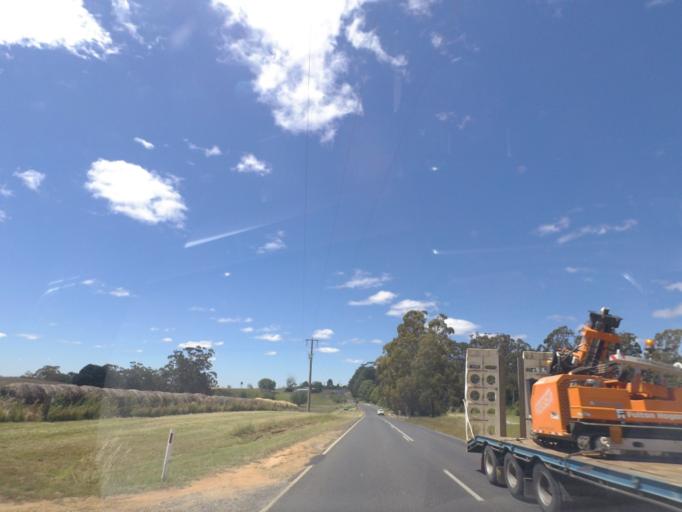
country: AU
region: Victoria
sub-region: Mount Alexander
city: Castlemaine
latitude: -37.3263
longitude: 144.1920
